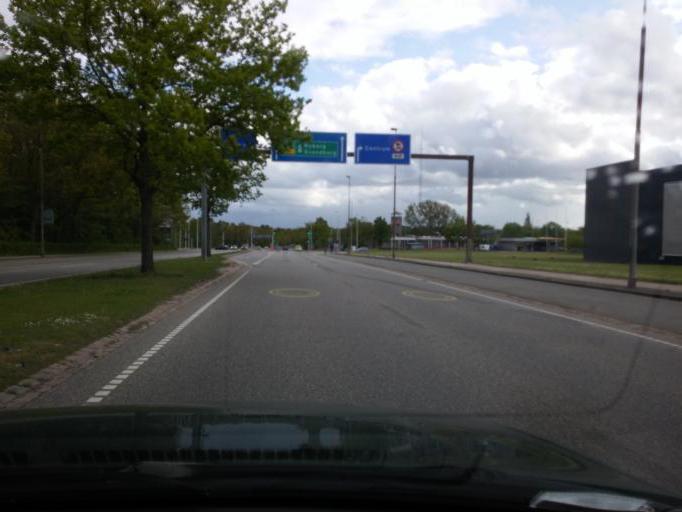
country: DK
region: South Denmark
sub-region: Odense Kommune
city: Seden
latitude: 55.4033
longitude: 10.4254
